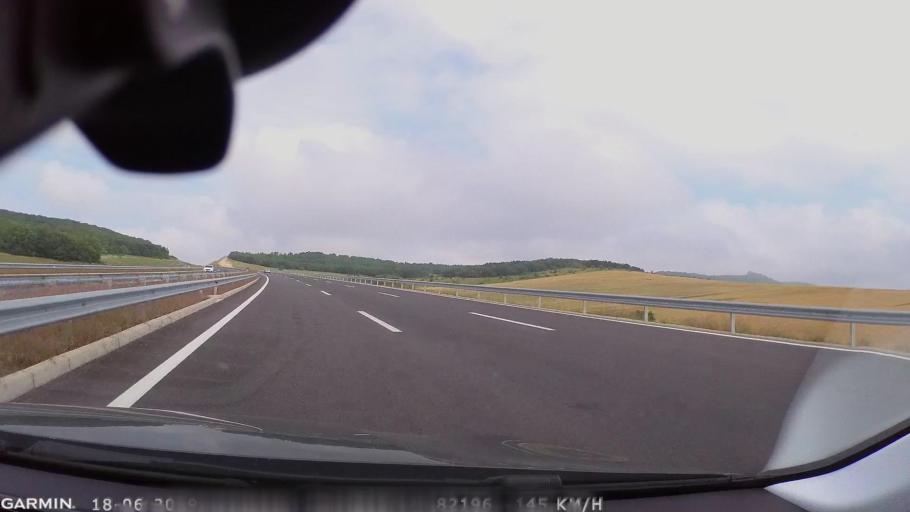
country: MK
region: Sveti Nikole
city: Gorobinci
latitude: 41.9189
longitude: 21.8733
